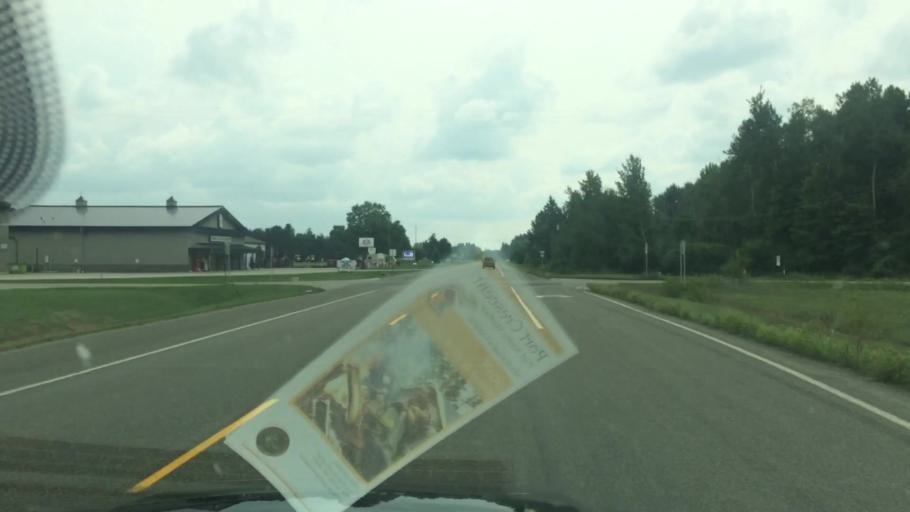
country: US
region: Michigan
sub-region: Tuscola County
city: Cass City
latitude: 43.6617
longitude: -83.0983
